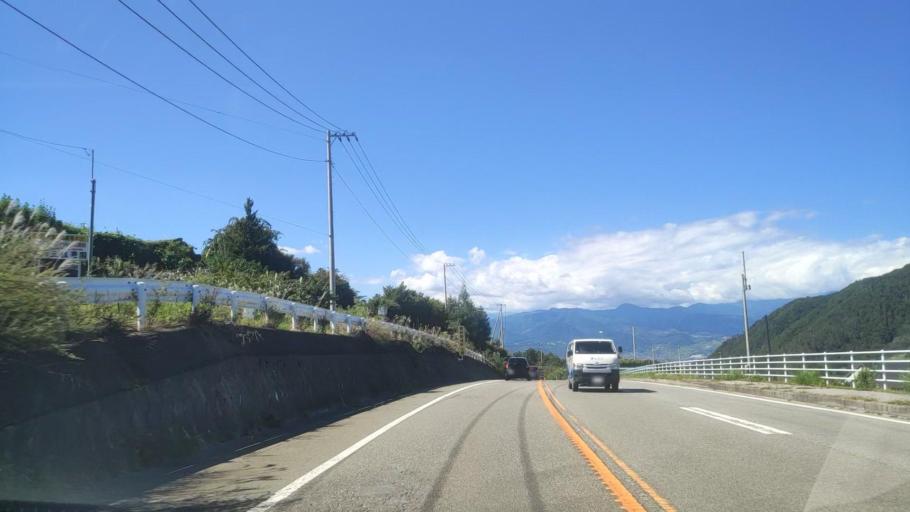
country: JP
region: Yamanashi
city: Isawa
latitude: 35.5969
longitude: 138.7120
